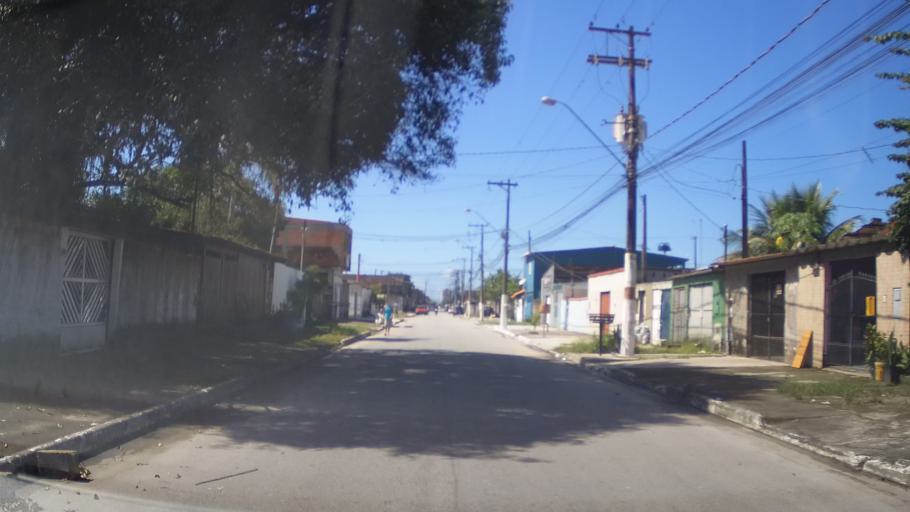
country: BR
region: Sao Paulo
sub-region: Mongagua
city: Mongagua
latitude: -24.0326
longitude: -46.5363
